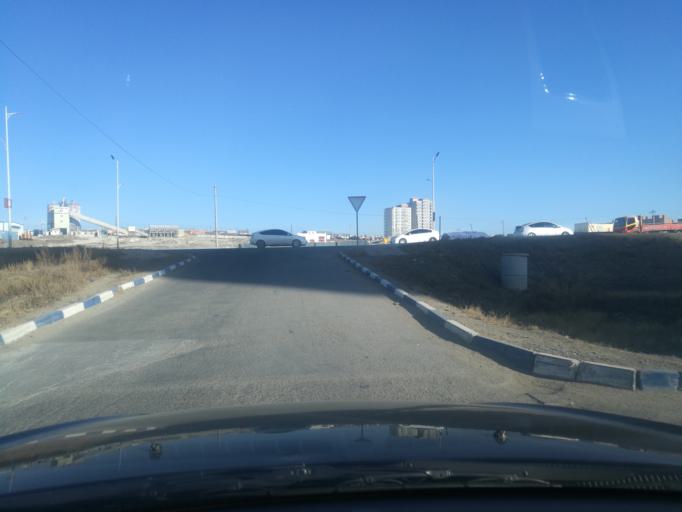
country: MN
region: Ulaanbaatar
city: Ulaanbaatar
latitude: 47.8560
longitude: 106.7800
